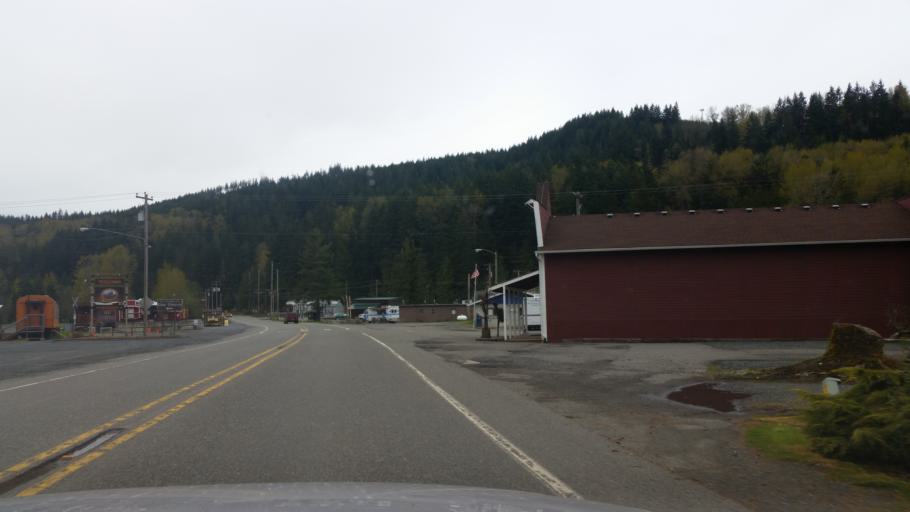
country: US
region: Washington
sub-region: Pierce County
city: Eatonville
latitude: 46.7641
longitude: -122.1934
